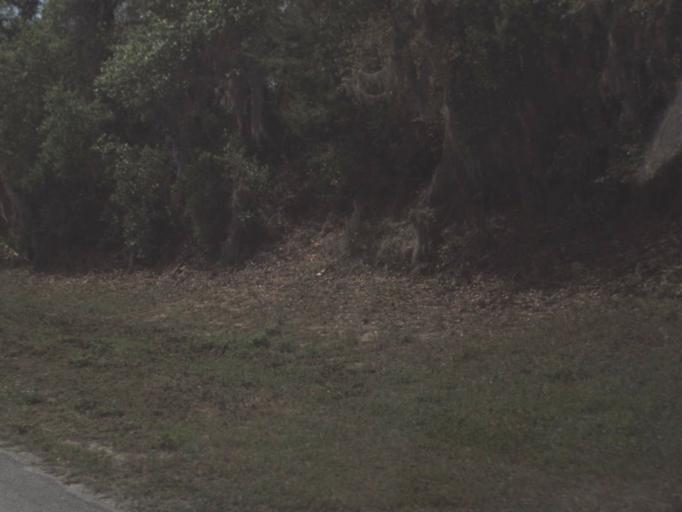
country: US
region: Florida
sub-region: Lake County
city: Astor
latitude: 29.2788
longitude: -81.6483
